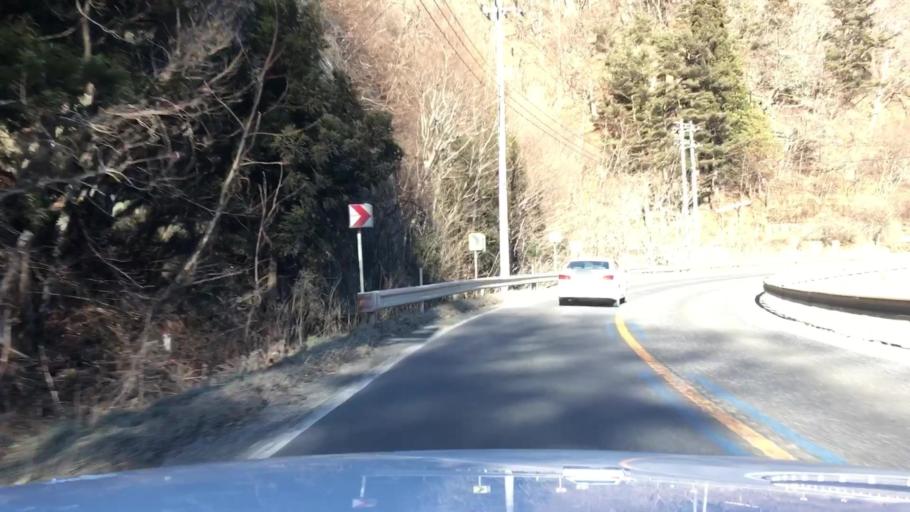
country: JP
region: Iwate
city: Miyako
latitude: 39.6055
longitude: 141.7721
